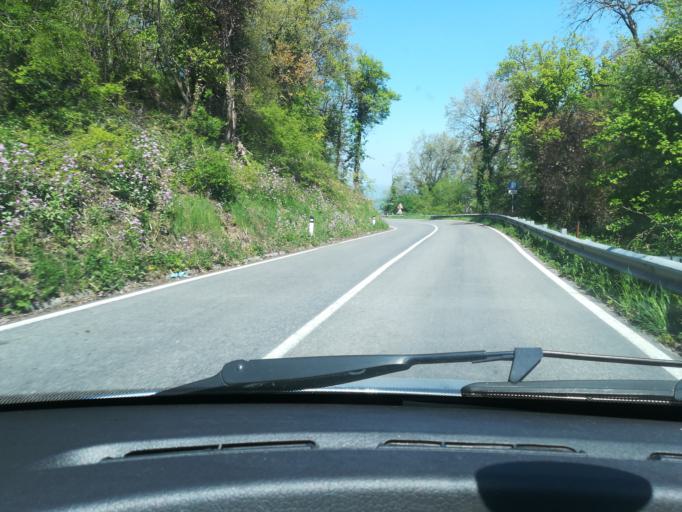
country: IT
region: The Marches
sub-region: Provincia di Macerata
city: Cingoli
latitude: 43.3798
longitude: 13.2114
